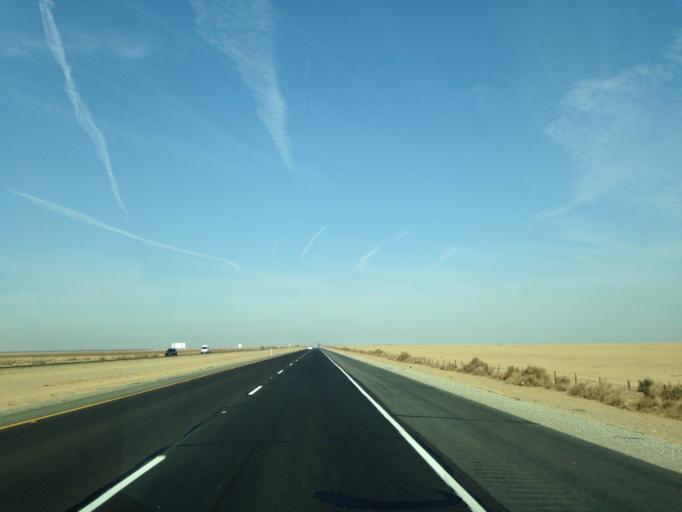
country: US
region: California
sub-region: Kern County
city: Lost Hills
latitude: 35.6325
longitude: -119.6651
